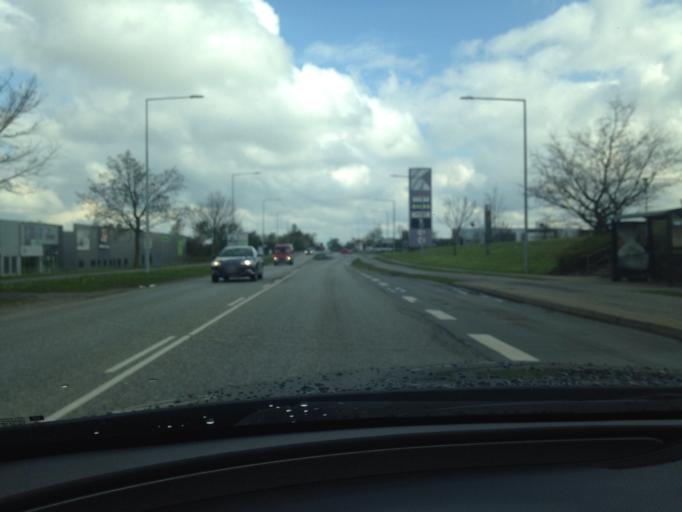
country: DK
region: South Denmark
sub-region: Kolding Kommune
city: Kolding
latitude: 55.5146
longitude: 9.4576
